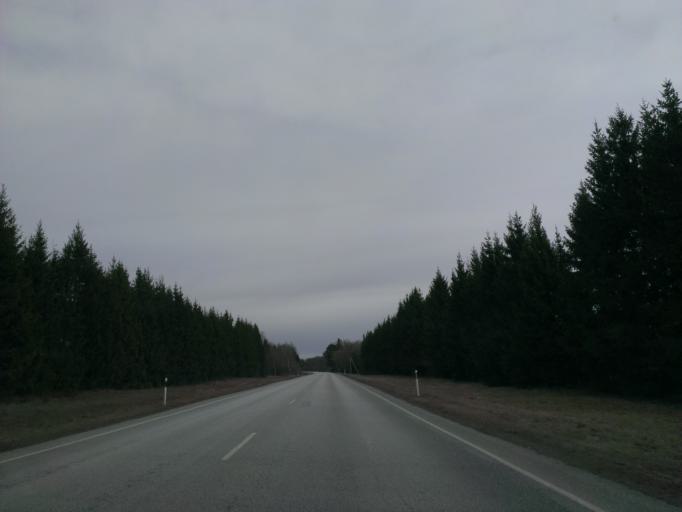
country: EE
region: Laeaene
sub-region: Lihula vald
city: Lihula
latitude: 58.6100
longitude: 23.5742
